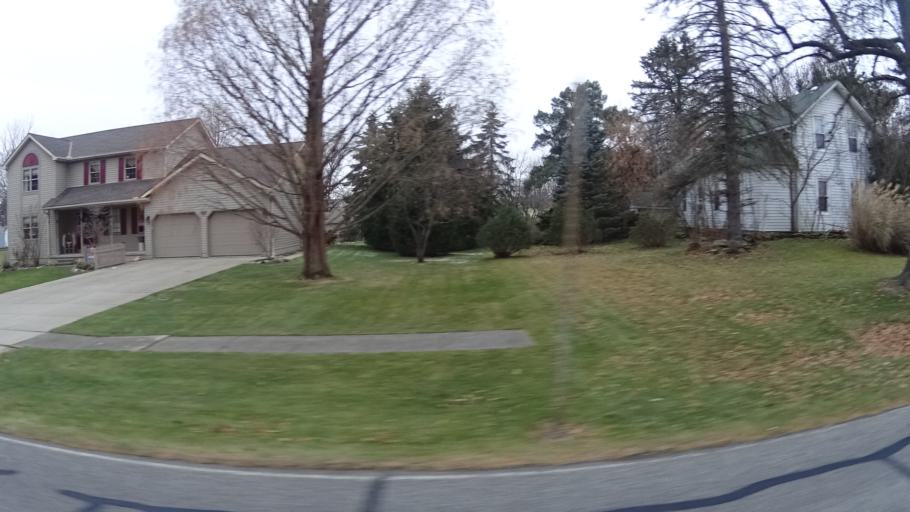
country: US
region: Ohio
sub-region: Lorain County
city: Grafton
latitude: 41.2737
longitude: -82.0513
